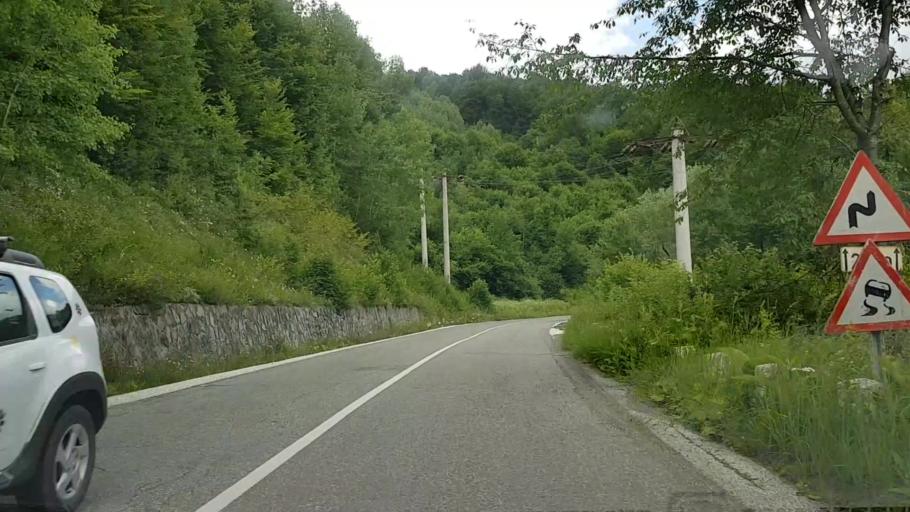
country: RO
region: Neamt
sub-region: Comuna Pangarati
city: Pangarati
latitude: 46.9581
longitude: 26.1235
